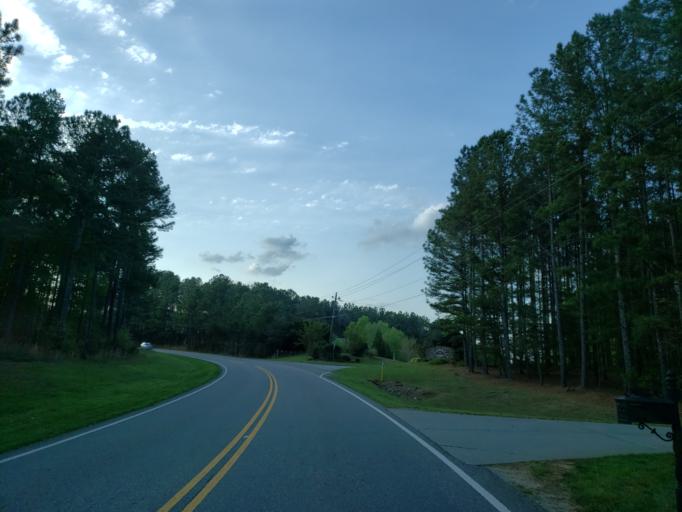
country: US
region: Georgia
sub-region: Cherokee County
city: Ball Ground
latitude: 34.2693
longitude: -84.3661
